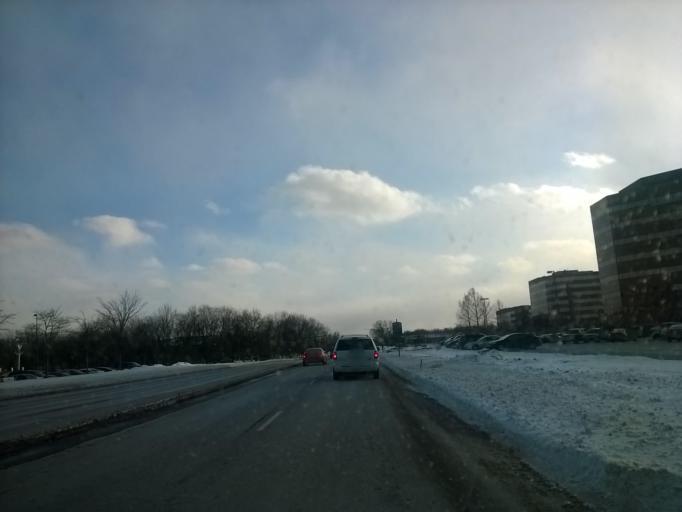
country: US
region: Indiana
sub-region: Hamilton County
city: Carmel
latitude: 39.9582
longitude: -86.1552
